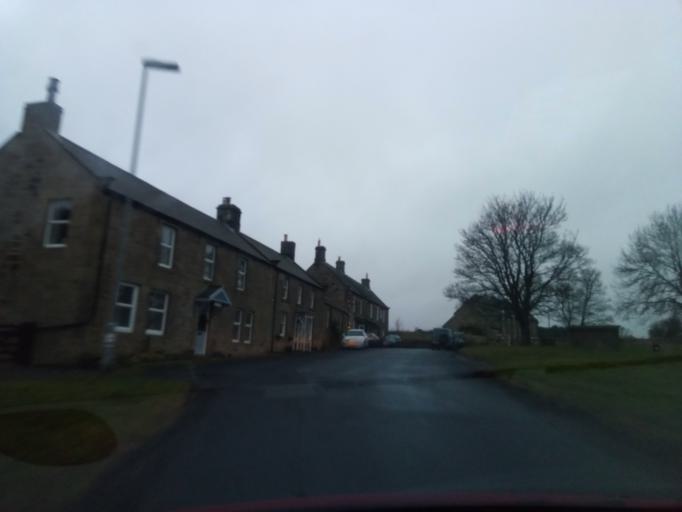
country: GB
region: England
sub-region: Northumberland
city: Otterburn
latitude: 55.2324
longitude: -2.1022
